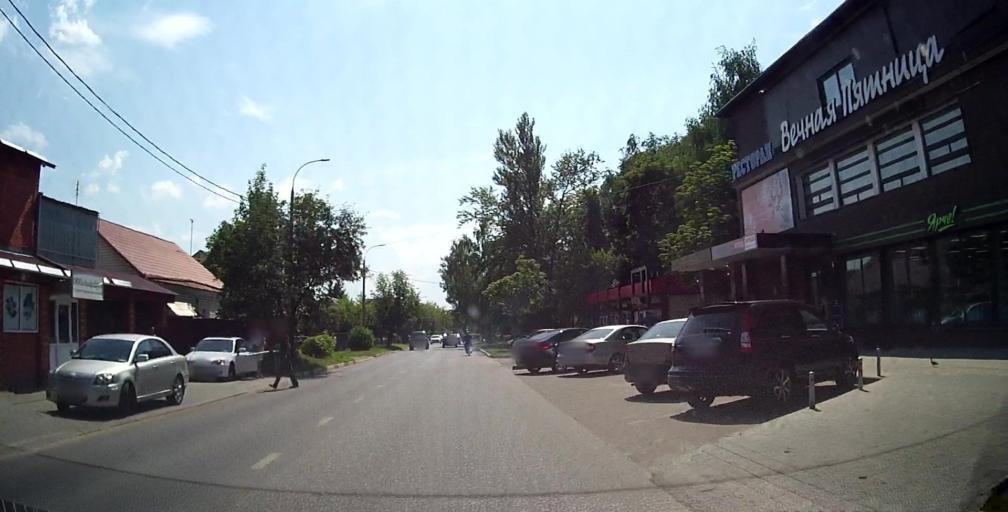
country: RU
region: Moskovskaya
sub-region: Podol'skiy Rayon
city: Podol'sk
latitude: 55.4136
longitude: 37.5267
